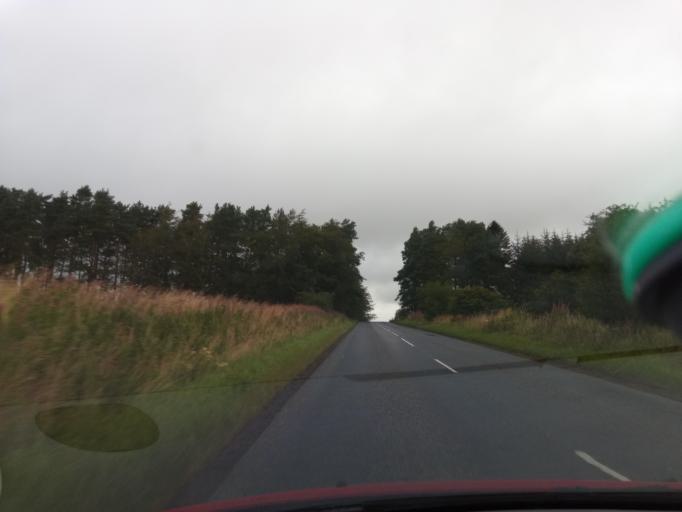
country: GB
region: Scotland
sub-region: The Scottish Borders
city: Earlston
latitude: 55.6631
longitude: -2.5518
